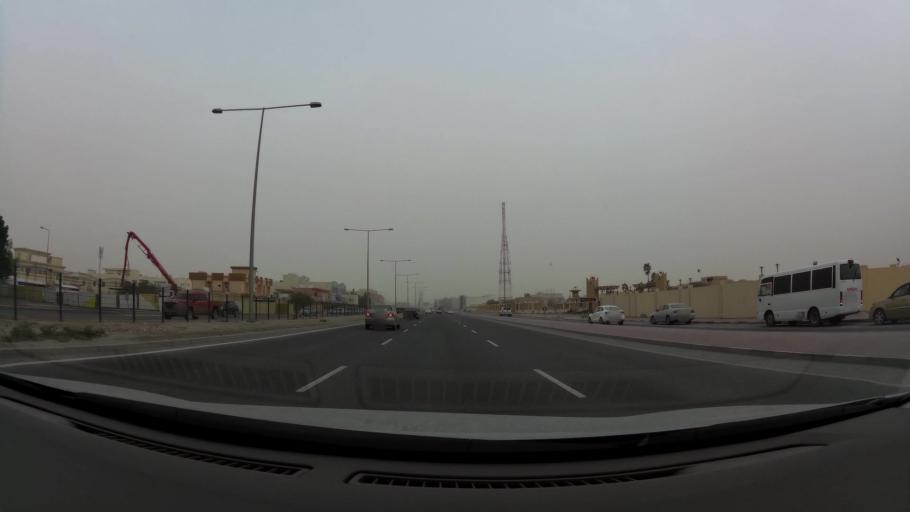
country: QA
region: Baladiyat ad Dawhah
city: Doha
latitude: 25.2332
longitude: 51.4847
